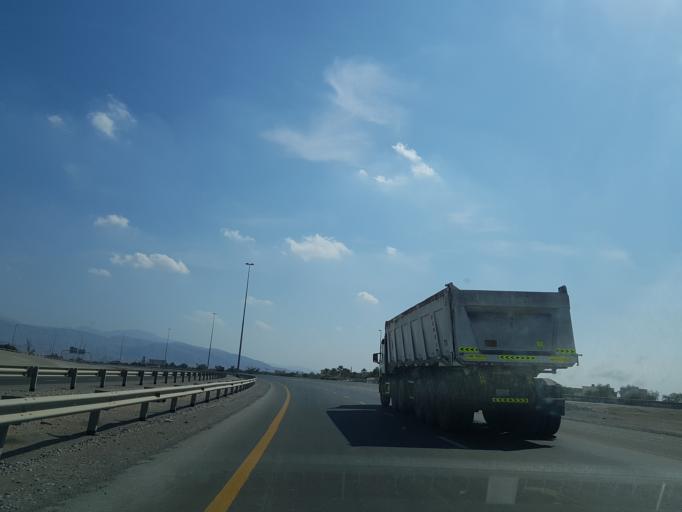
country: AE
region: Ra's al Khaymah
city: Ras al-Khaimah
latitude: 25.8326
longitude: 56.0158
